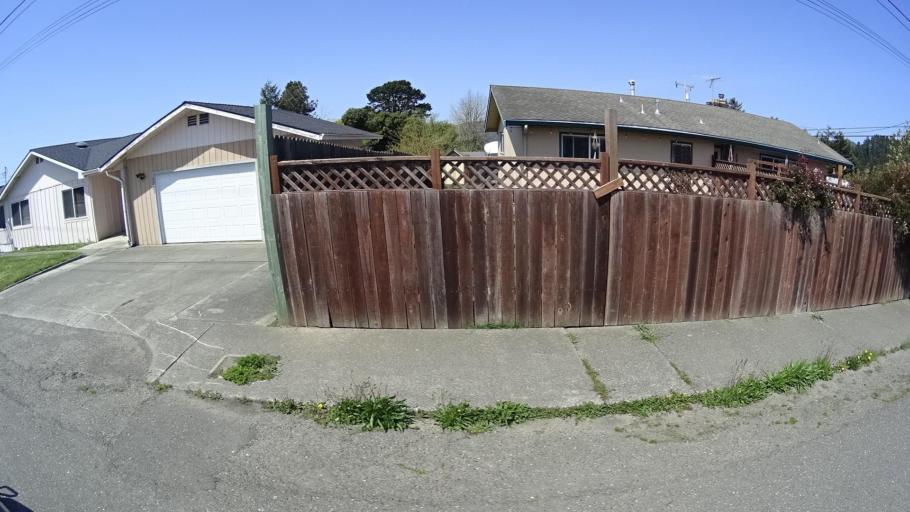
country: US
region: California
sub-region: Humboldt County
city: Hydesville
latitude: 40.5630
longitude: -124.1317
